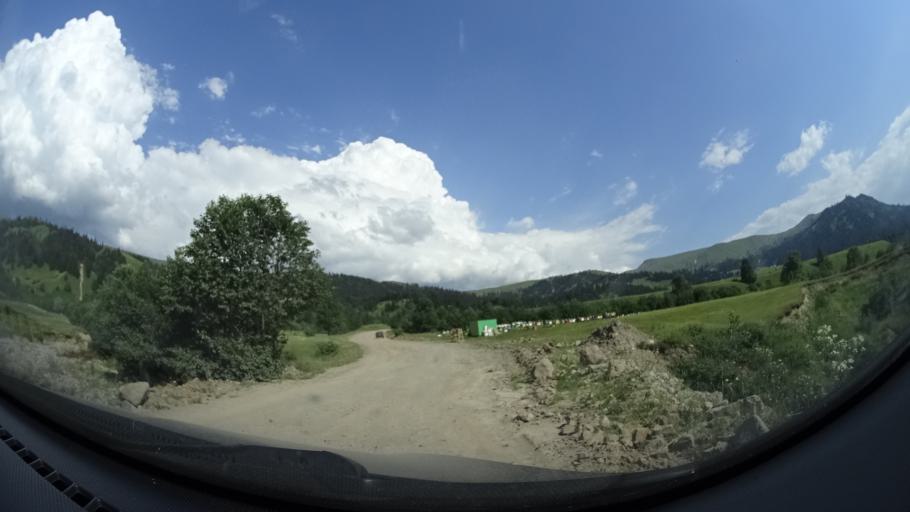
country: GE
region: Ajaria
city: Dioknisi
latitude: 41.6453
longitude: 42.4887
